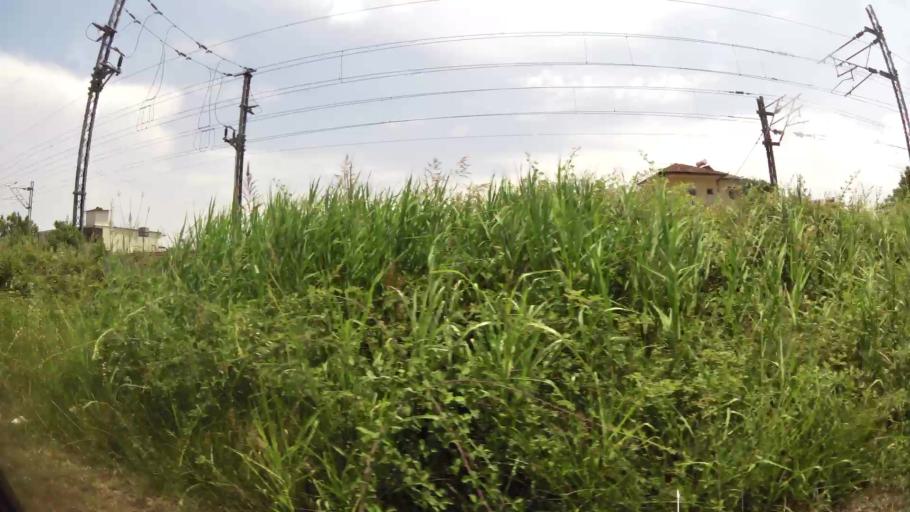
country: GR
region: Central Macedonia
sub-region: Nomos Pierias
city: Peristasi
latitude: 40.2773
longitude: 22.5398
